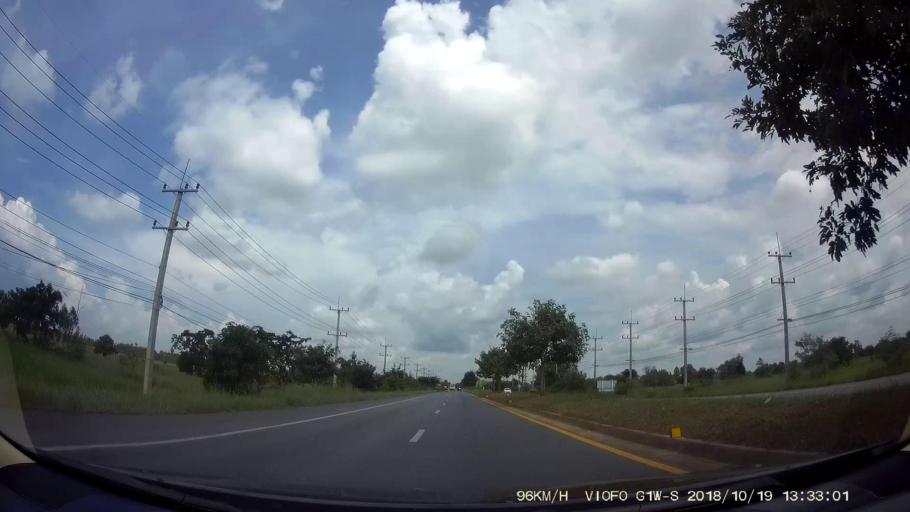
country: TH
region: Chaiyaphum
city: Chatturat
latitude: 15.5775
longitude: 101.8908
